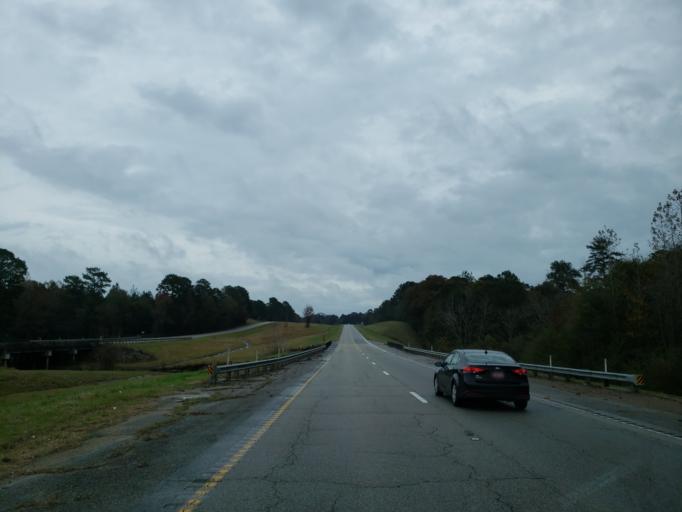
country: US
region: Mississippi
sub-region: Jones County
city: Sharon
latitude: 31.6997
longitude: -88.9012
